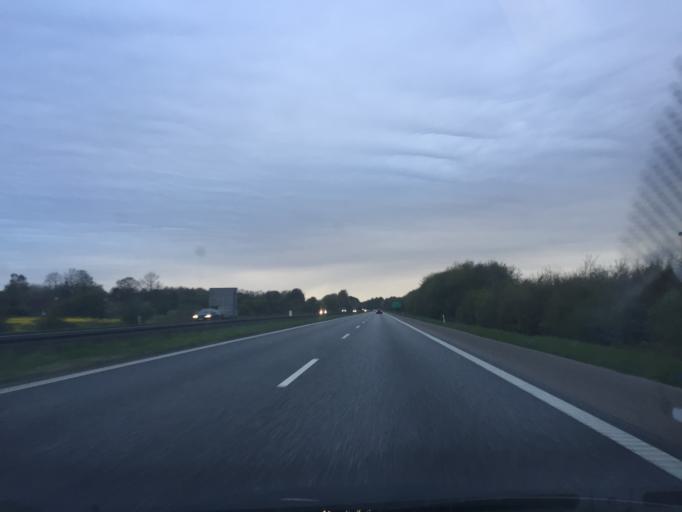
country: DK
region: South Denmark
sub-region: Fredericia Kommune
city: Taulov
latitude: 55.5399
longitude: 9.6257
